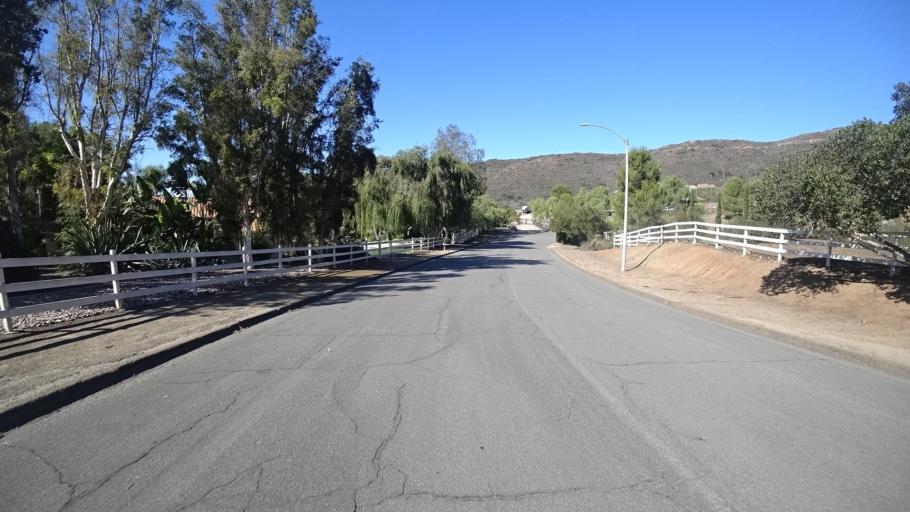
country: US
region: California
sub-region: San Diego County
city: Jamul
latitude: 32.7402
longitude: -116.8599
